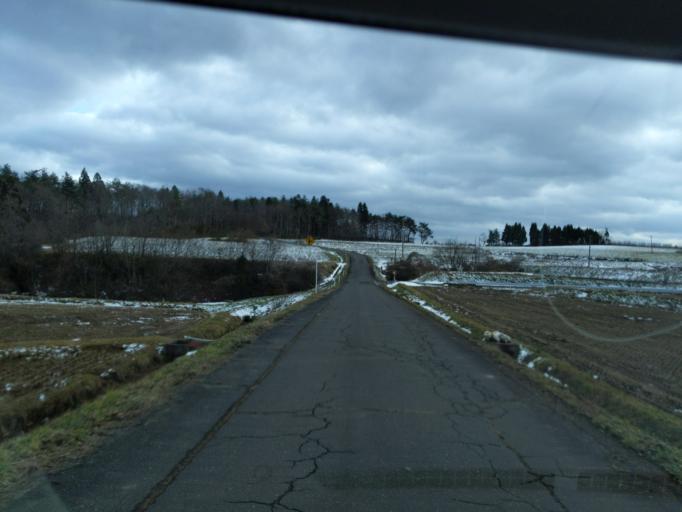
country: JP
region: Iwate
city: Ichinoseki
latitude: 38.9902
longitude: 141.0009
